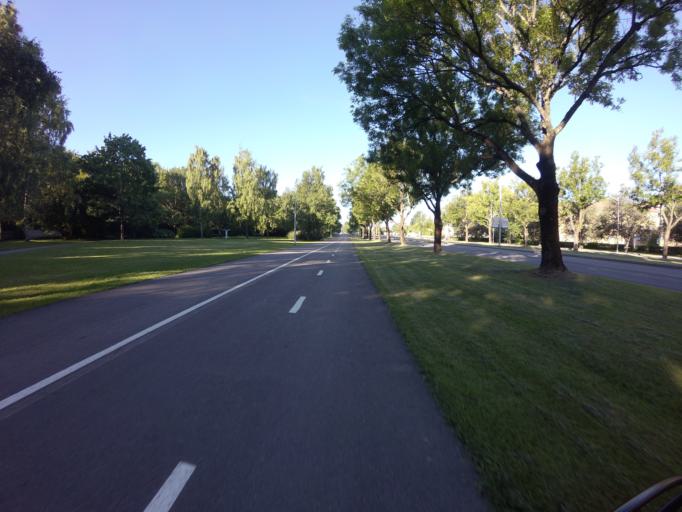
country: FI
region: Varsinais-Suomi
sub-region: Turku
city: Turku
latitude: 60.4661
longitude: 22.2750
